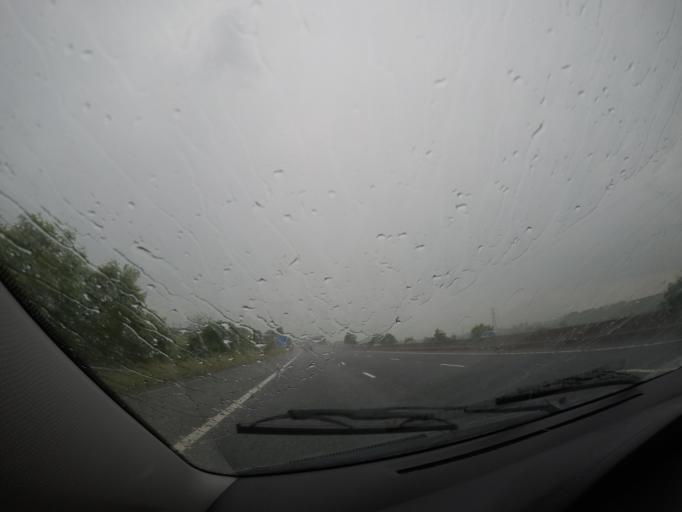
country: GB
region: England
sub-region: Cumbria
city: Penrith
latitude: 54.6760
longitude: -2.7798
